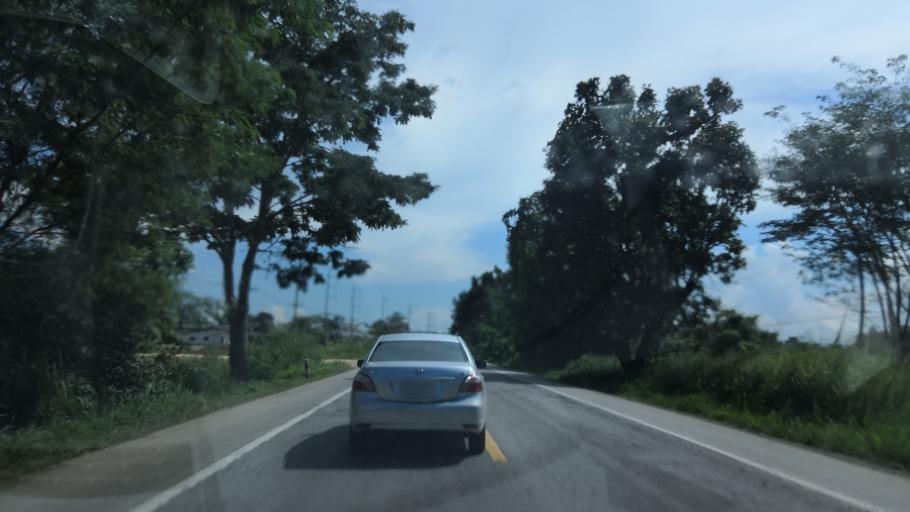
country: TH
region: Chiang Rai
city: Wiang Pa Pao
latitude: 19.4031
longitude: 99.5014
